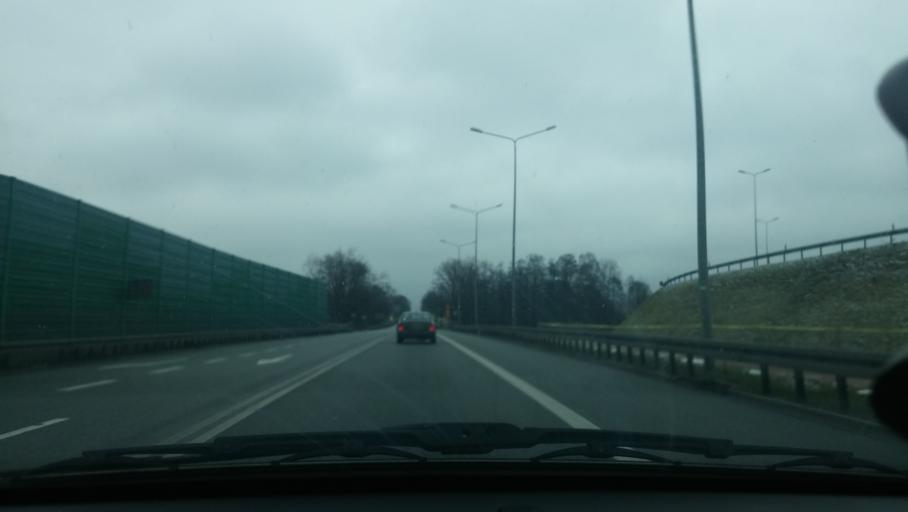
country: PL
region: Masovian Voivodeship
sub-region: Powiat minski
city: Kaluszyn
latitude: 52.1993
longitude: 21.7740
